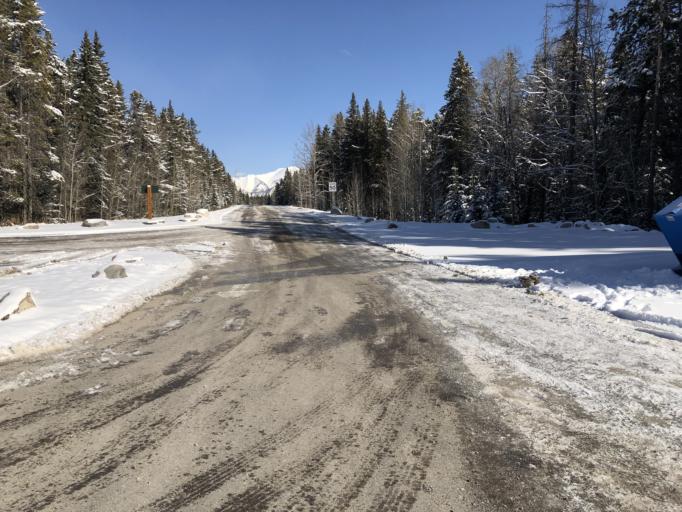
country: CA
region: Alberta
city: Banff
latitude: 51.1997
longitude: -115.4898
